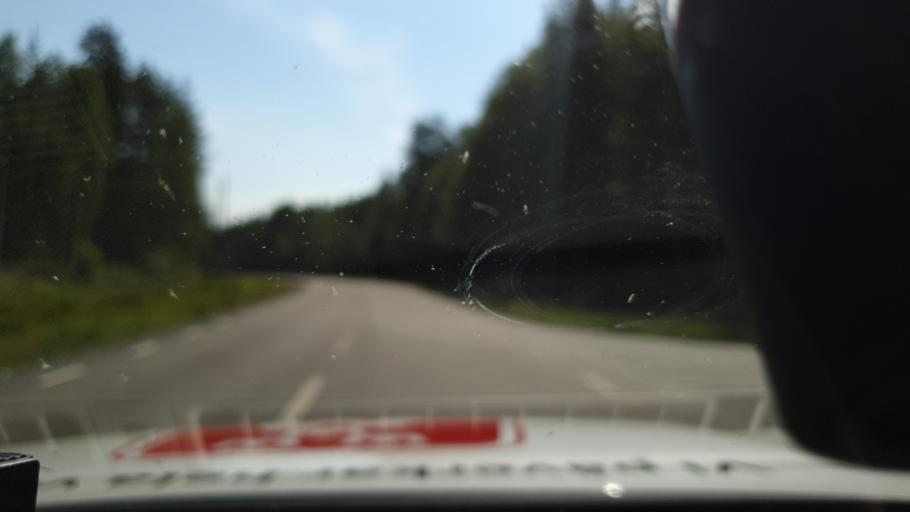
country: SE
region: Norrbotten
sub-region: Lulea Kommun
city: Sodra Sunderbyn
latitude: 65.8204
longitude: 21.8959
